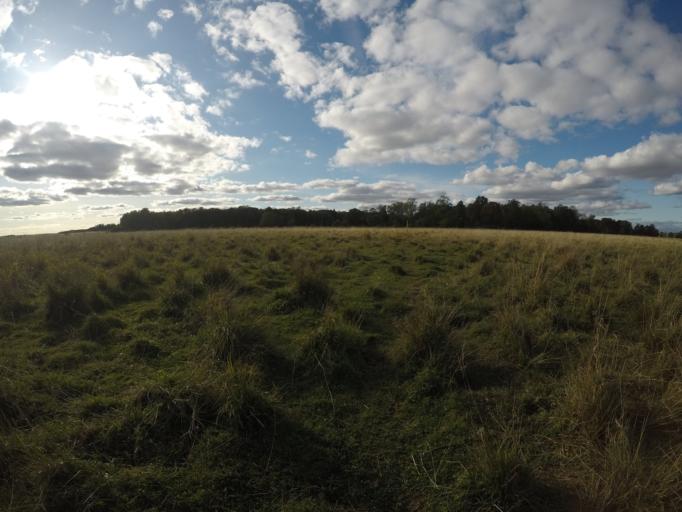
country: SE
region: Vaestmanland
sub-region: Hallstahammars Kommun
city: Kolback
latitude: 59.4785
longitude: 16.2205
